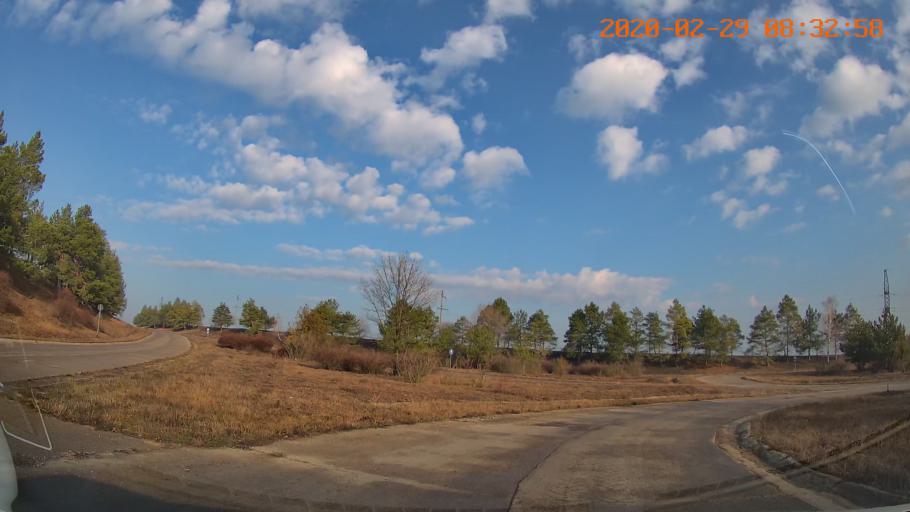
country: MD
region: Anenii Noi
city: Anenii Noi
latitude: 46.9277
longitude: 29.2857
